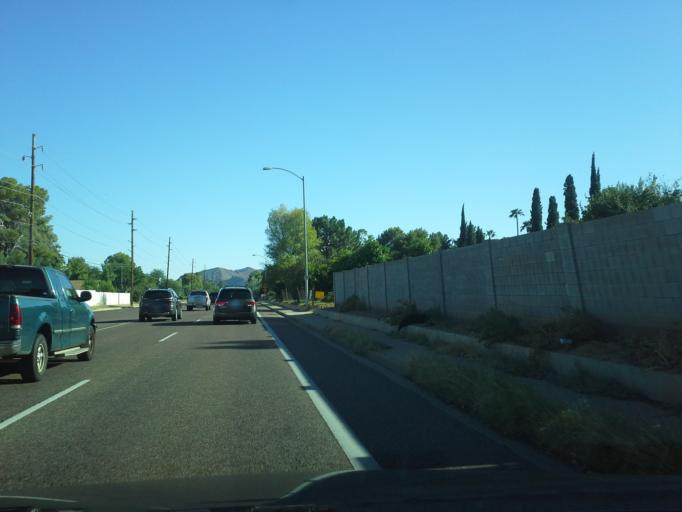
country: US
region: Arizona
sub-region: Maricopa County
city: Paradise Valley
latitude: 33.6093
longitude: -111.9606
